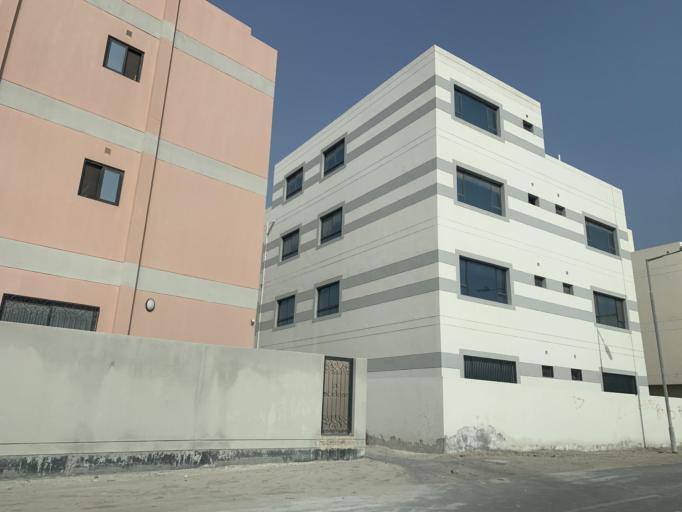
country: BH
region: Northern
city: Madinat `Isa
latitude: 26.1884
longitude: 50.5605
